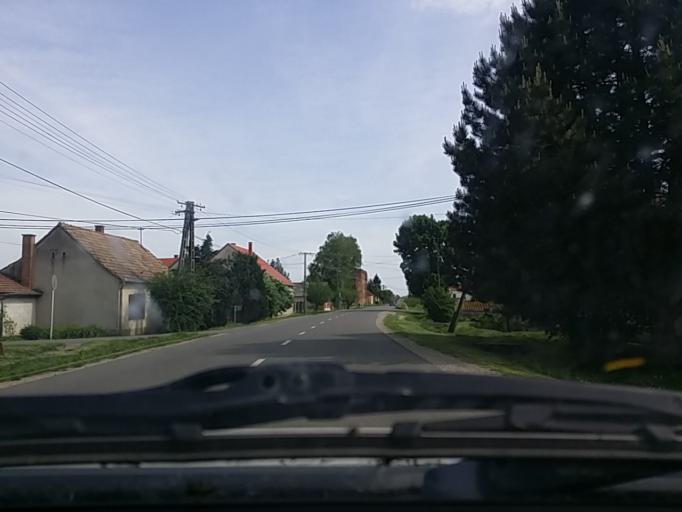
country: HR
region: Osjecko-Baranjska
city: Viljevo
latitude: 45.8278
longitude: 18.0970
